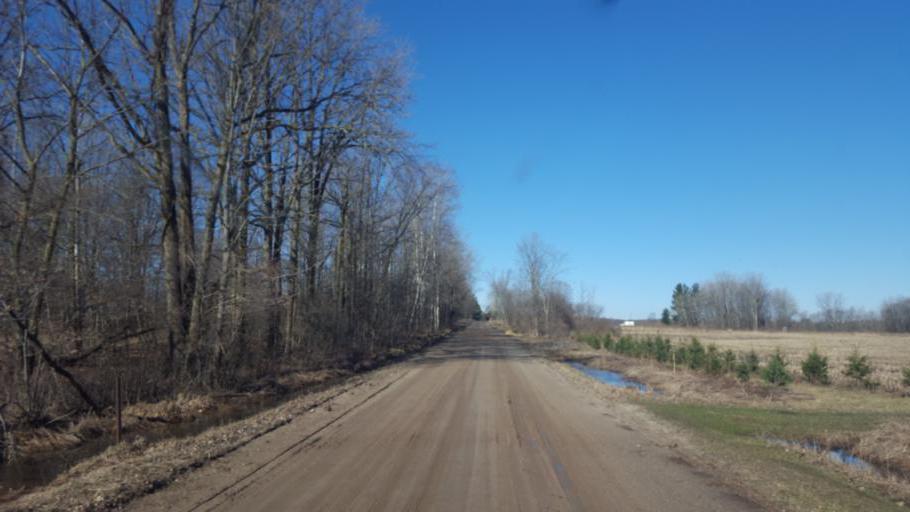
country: US
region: Michigan
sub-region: Isabella County
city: Lake Isabella
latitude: 43.5382
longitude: -85.0210
